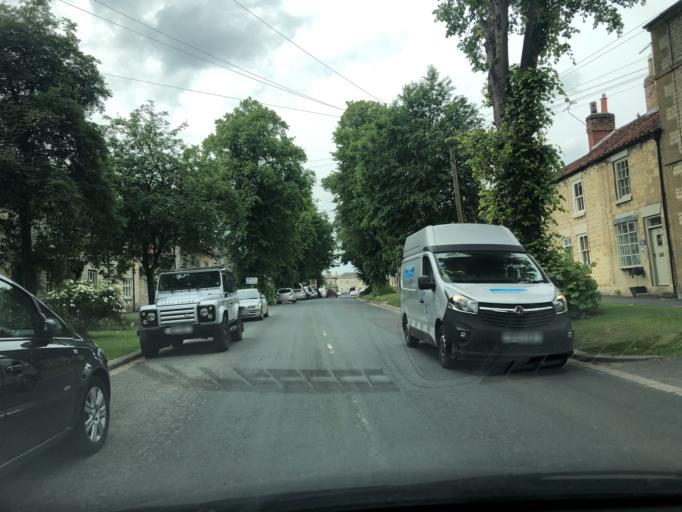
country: GB
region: England
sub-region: North Yorkshire
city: Pickering
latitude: 54.2426
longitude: -0.7722
